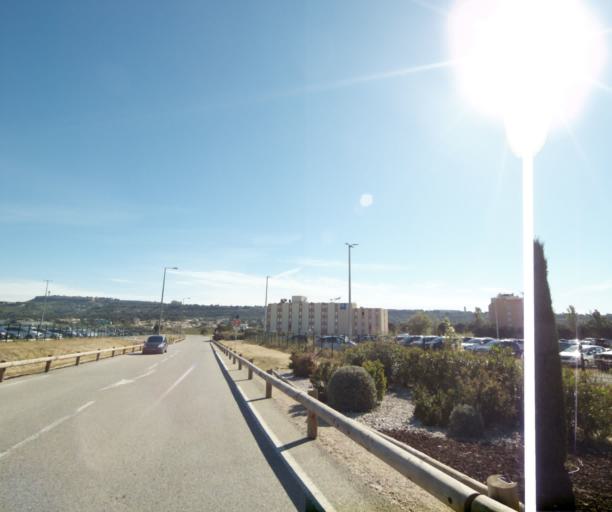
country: FR
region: Provence-Alpes-Cote d'Azur
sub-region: Departement des Bouches-du-Rhone
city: Saint-Victoret
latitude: 43.4458
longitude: 5.2237
